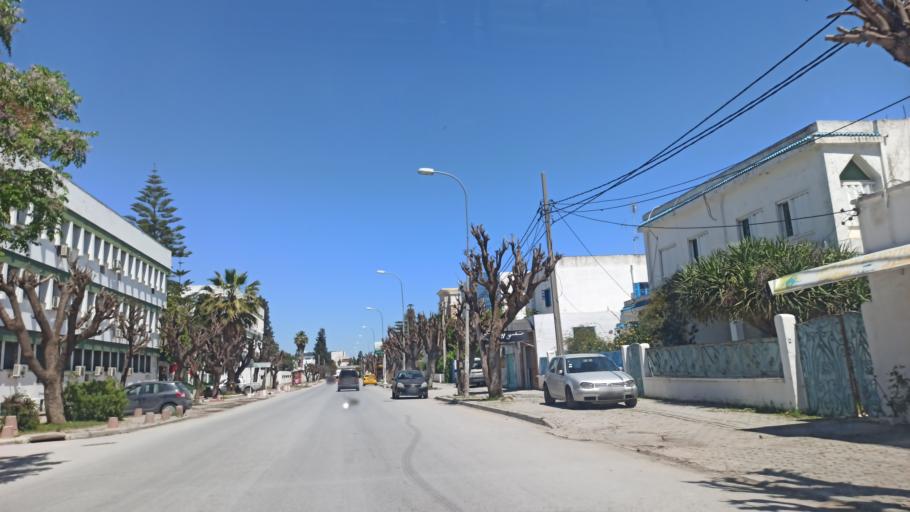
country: TN
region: Tunis
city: Tunis
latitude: 36.8275
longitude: 10.1842
